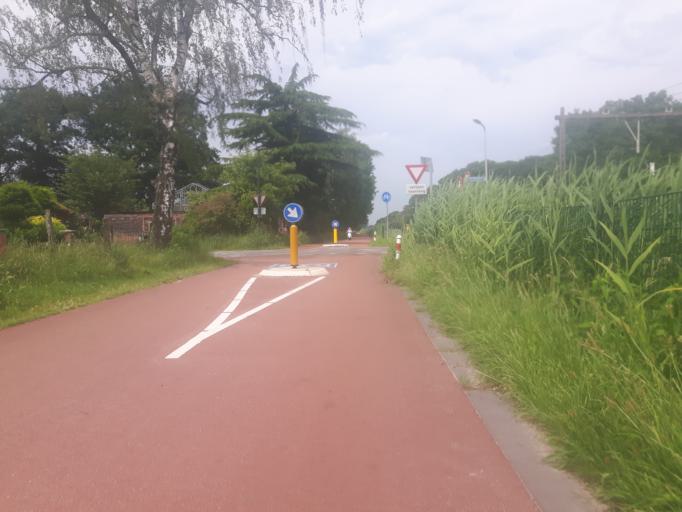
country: NL
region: Overijssel
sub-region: Gemeente Hengelo
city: Hengelo
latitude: 52.2478
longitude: 6.8219
